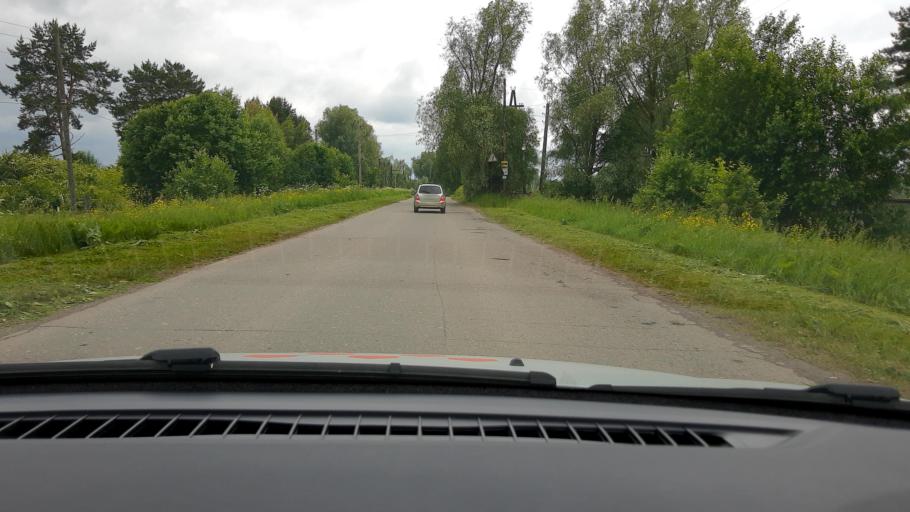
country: RU
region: Nizjnij Novgorod
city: Bogorodsk
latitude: 56.0782
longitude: 43.5109
